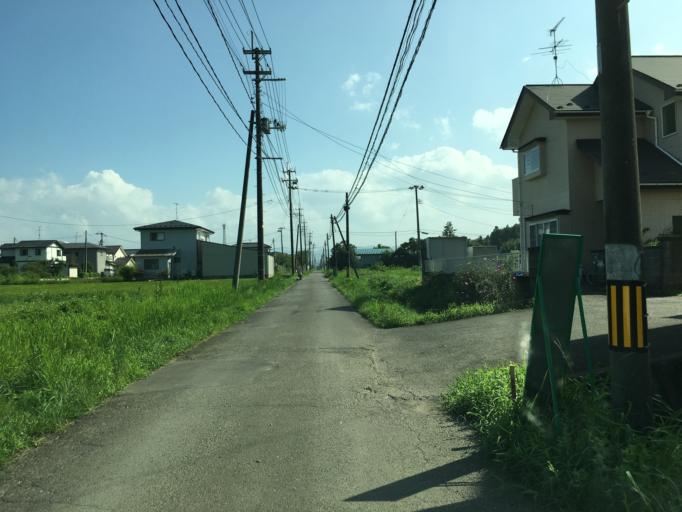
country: JP
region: Miyagi
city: Kakuda
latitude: 37.9584
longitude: 140.7809
